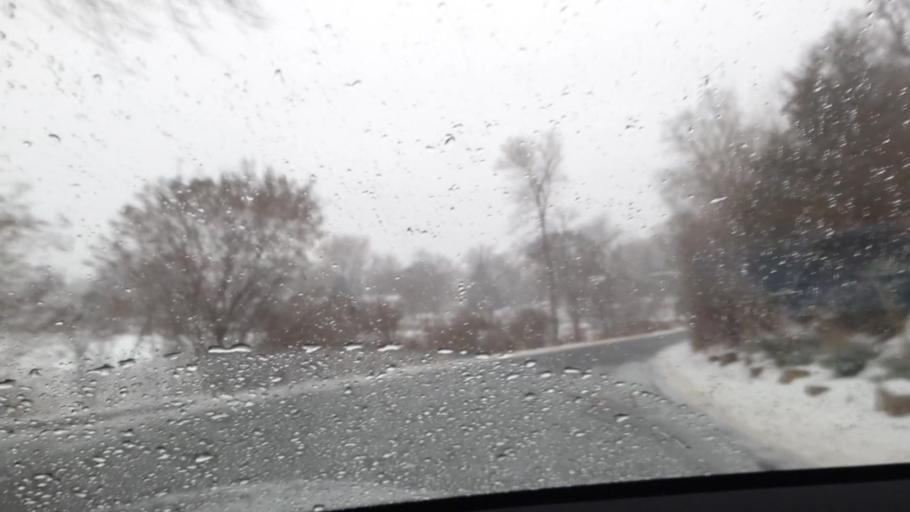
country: US
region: Wisconsin
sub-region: Saint Croix County
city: North Hudson
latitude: 44.9895
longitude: -92.7518
